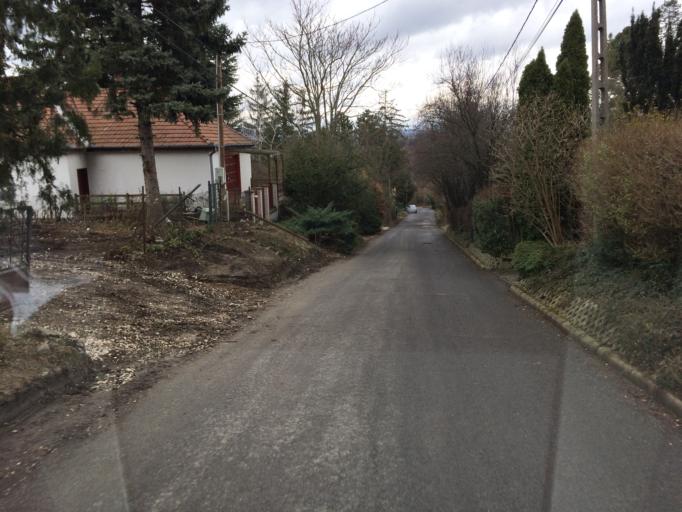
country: HU
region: Pest
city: Leanyfalu
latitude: 47.7258
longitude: 19.0838
